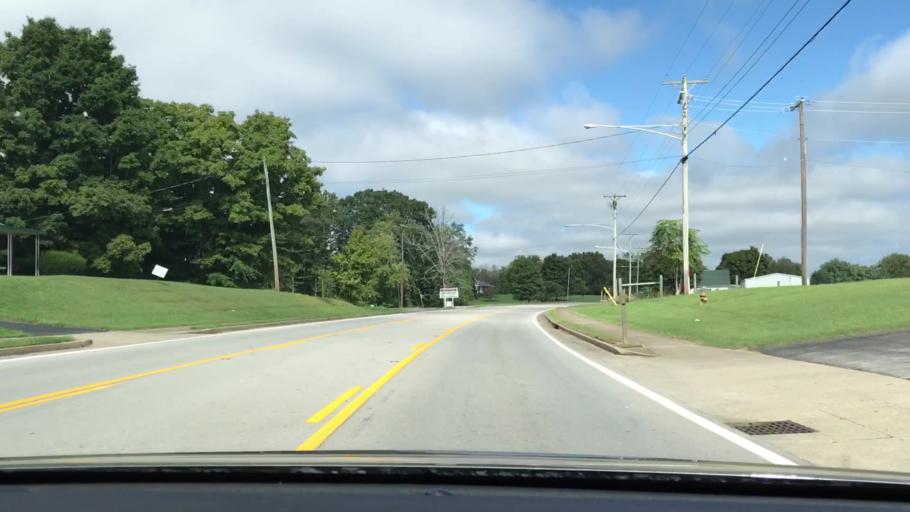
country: US
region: Kentucky
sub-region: Russell County
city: Jamestown
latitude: 36.9946
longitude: -85.0713
